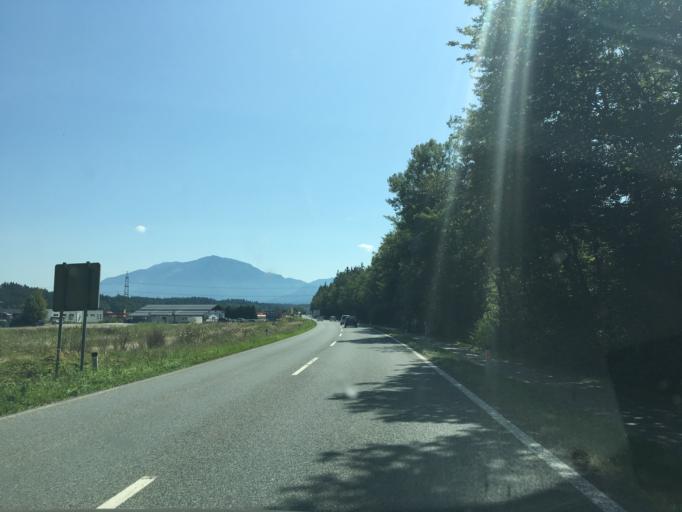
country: AT
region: Carinthia
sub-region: Politischer Bezirk Volkermarkt
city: Voelkermarkt
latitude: 46.6372
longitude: 14.6296
